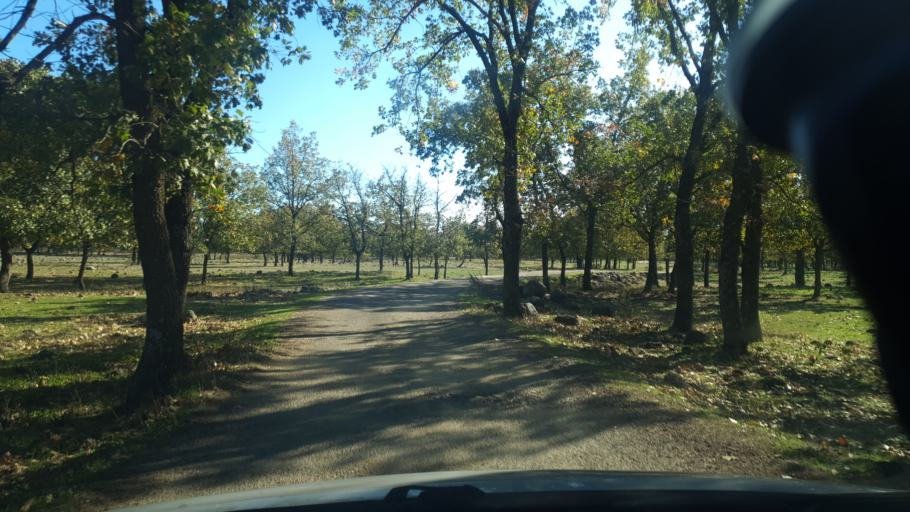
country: ES
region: Castille and Leon
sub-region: Provincia de Avila
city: Candeleda
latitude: 40.1215
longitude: -5.2656
